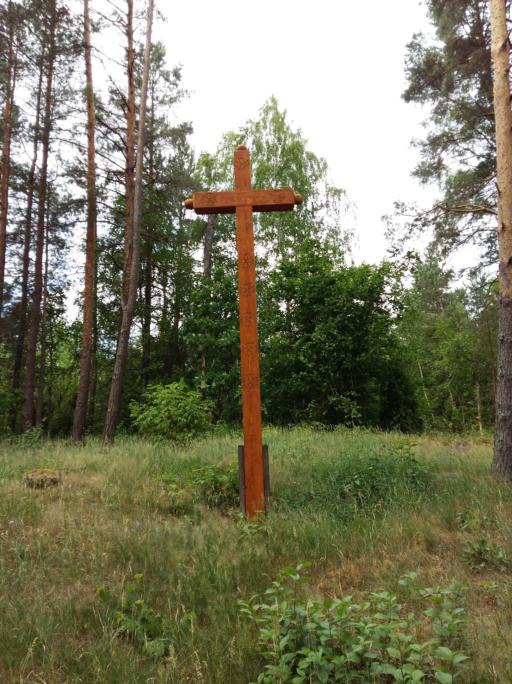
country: LT
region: Alytaus apskritis
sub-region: Alytaus rajonas
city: Daugai
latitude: 54.1720
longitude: 24.2197
